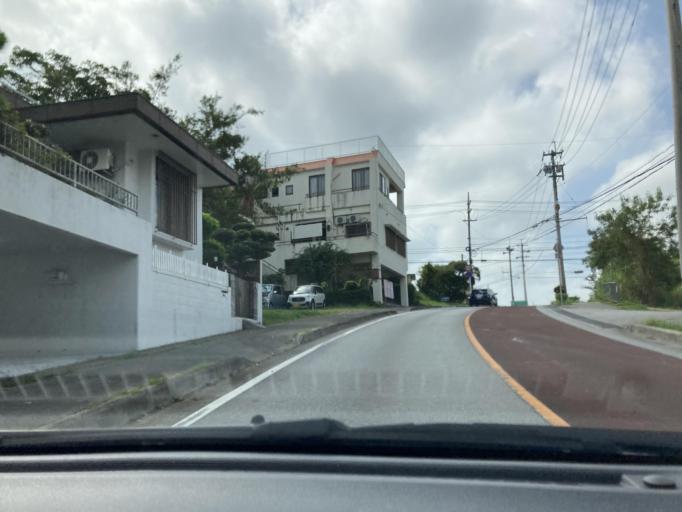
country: JP
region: Okinawa
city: Okinawa
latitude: 26.3185
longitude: 127.8048
